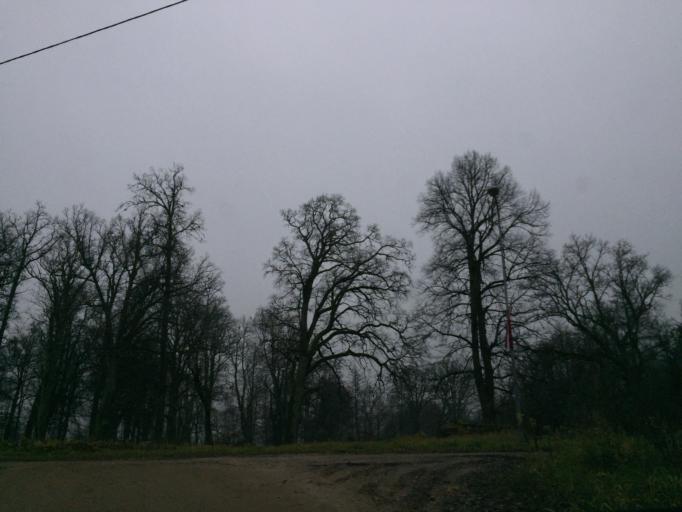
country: LV
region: Koceni
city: Koceni
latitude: 57.5237
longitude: 25.3327
